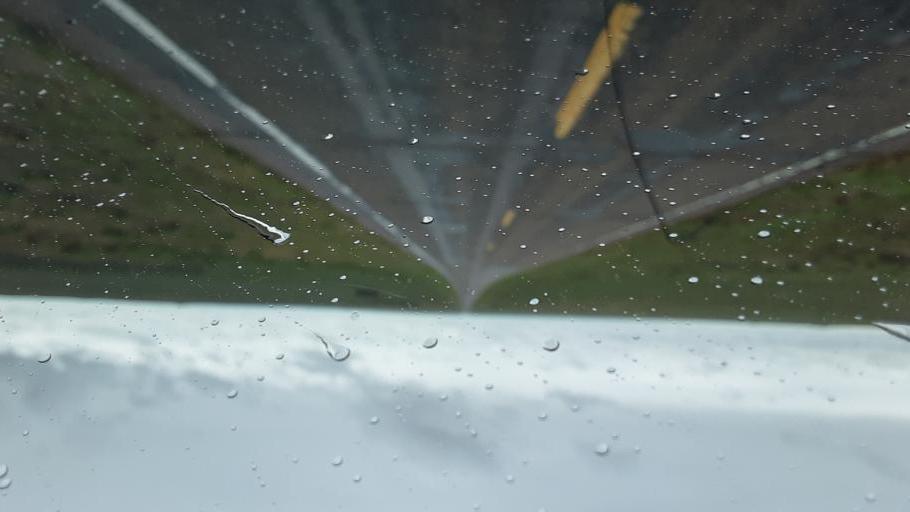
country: US
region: Colorado
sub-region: Lincoln County
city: Hugo
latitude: 38.8494
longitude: -103.2777
